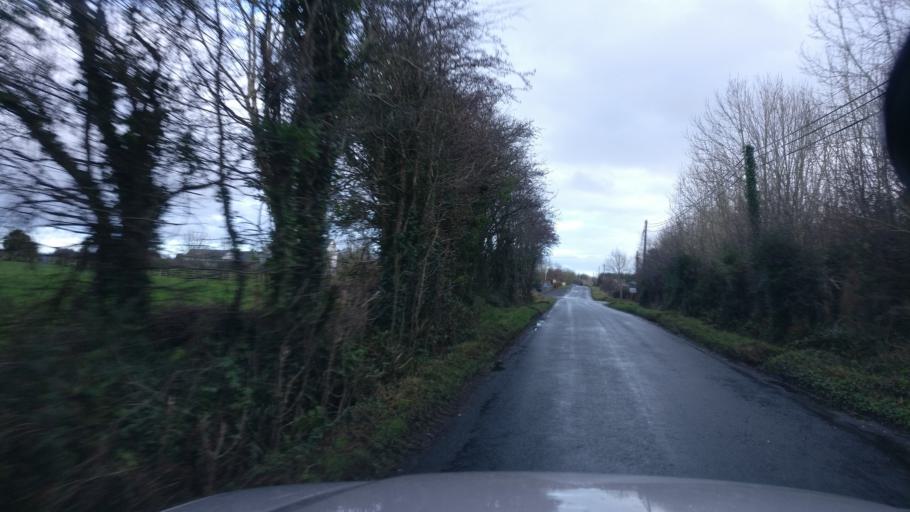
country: IE
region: Connaught
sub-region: County Galway
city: Athenry
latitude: 53.2992
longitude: -8.7147
